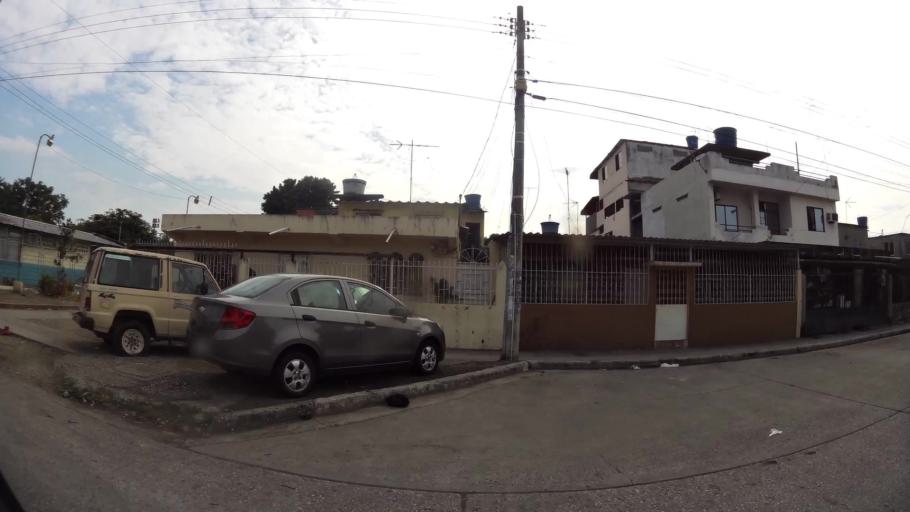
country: EC
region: Guayas
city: Guayaquil
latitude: -2.2527
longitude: -79.8851
